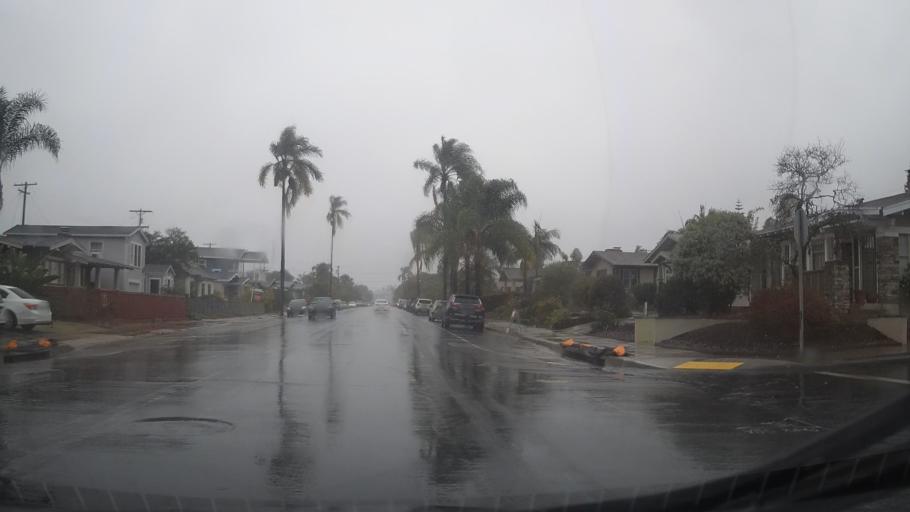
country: US
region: California
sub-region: San Diego County
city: San Diego
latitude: 32.7420
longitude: -117.1368
